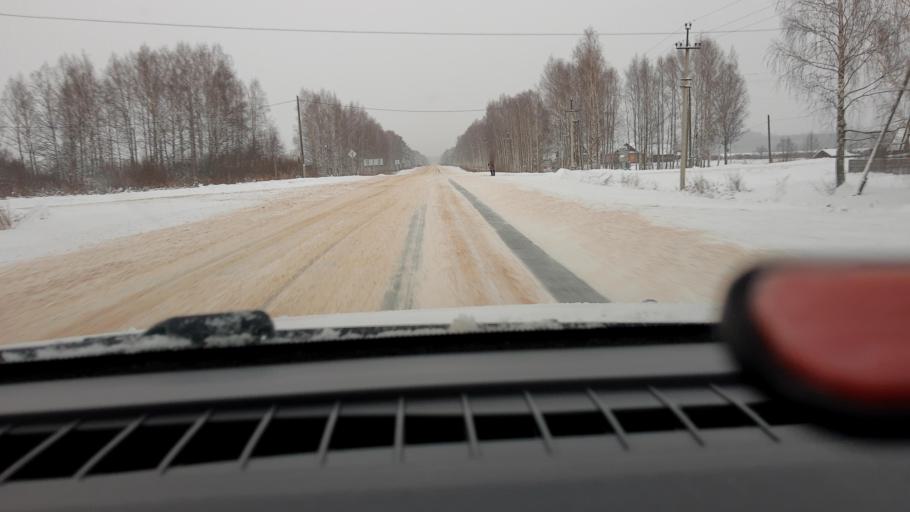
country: RU
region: Nizjnij Novgorod
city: Tonkino
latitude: 57.2715
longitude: 46.4610
